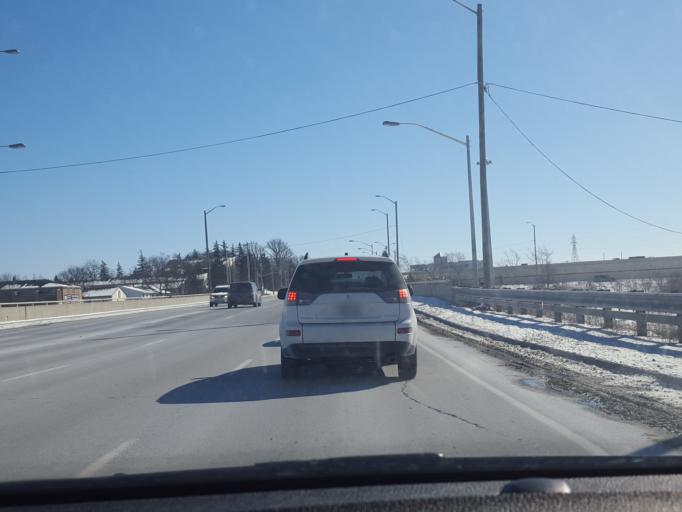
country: CA
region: Ontario
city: Kitchener
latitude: 43.4197
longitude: -80.5149
